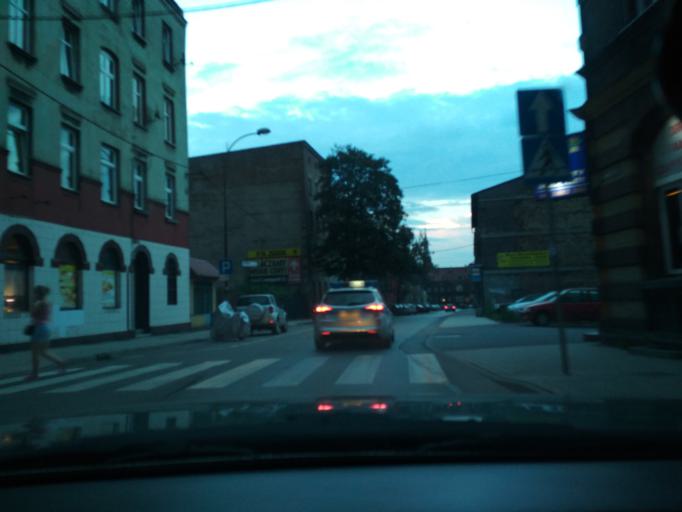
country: PL
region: Silesian Voivodeship
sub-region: Swietochlowice
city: Swietochlowice
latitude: 50.2899
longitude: 18.9183
